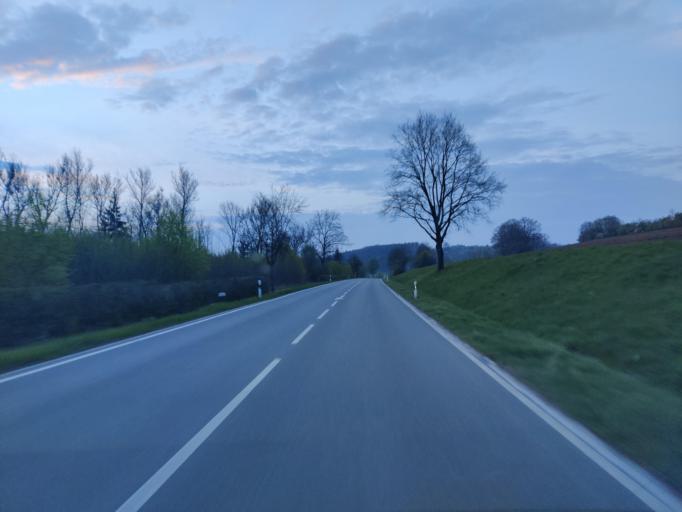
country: DE
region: Baden-Wuerttemberg
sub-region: Tuebingen Region
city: Dusslingen
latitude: 48.4623
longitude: 9.0732
